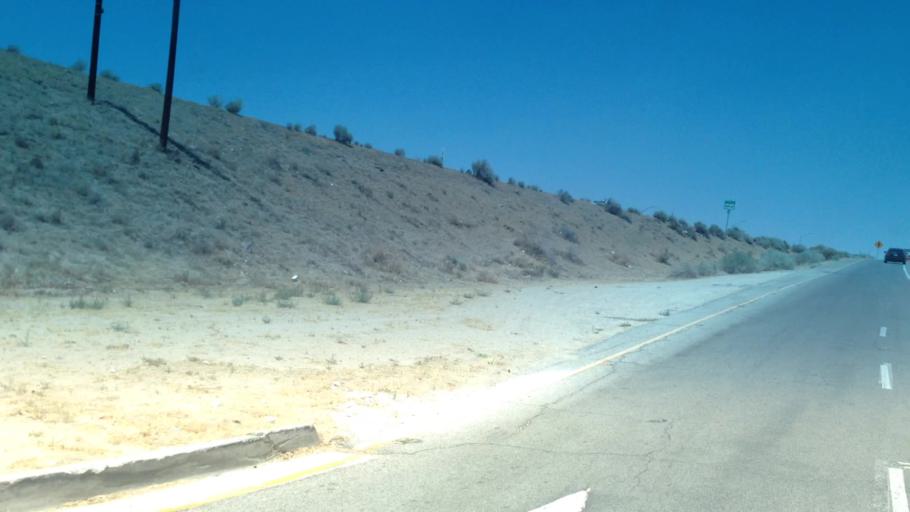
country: US
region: California
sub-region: Los Angeles County
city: Lancaster
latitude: 34.6896
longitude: -118.1692
